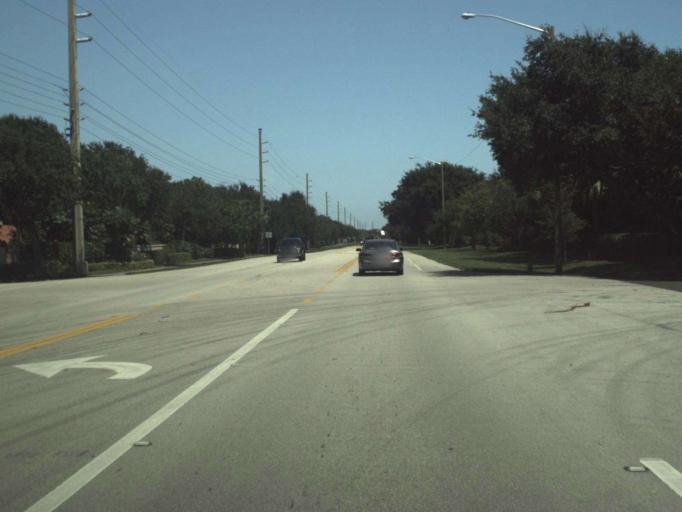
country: US
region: Florida
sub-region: Indian River County
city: South Beach
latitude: 27.6228
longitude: -80.3522
